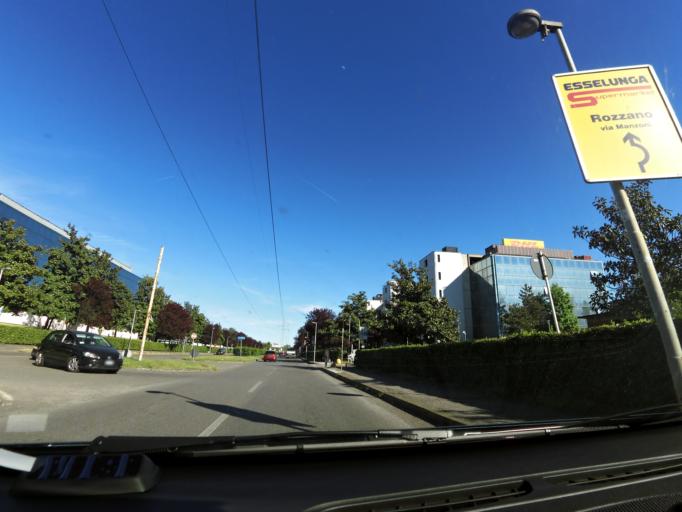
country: IT
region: Lombardy
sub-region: Citta metropolitana di Milano
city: Rozzano
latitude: 45.3969
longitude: 9.1467
